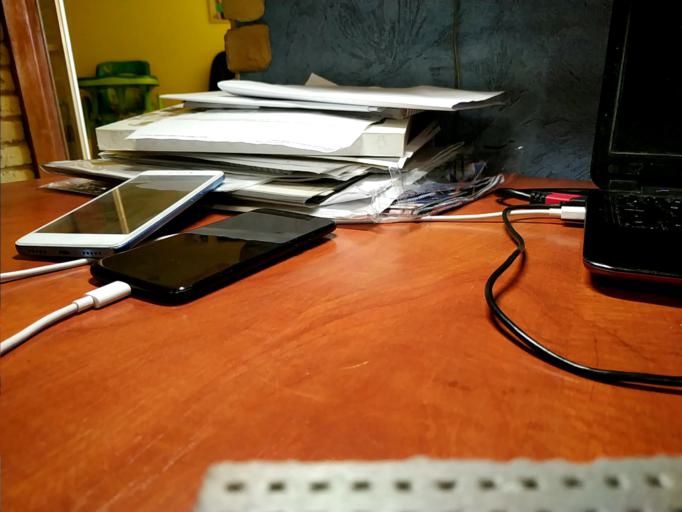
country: RU
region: Tverskaya
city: Kalashnikovo
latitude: 57.4087
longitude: 35.1801
